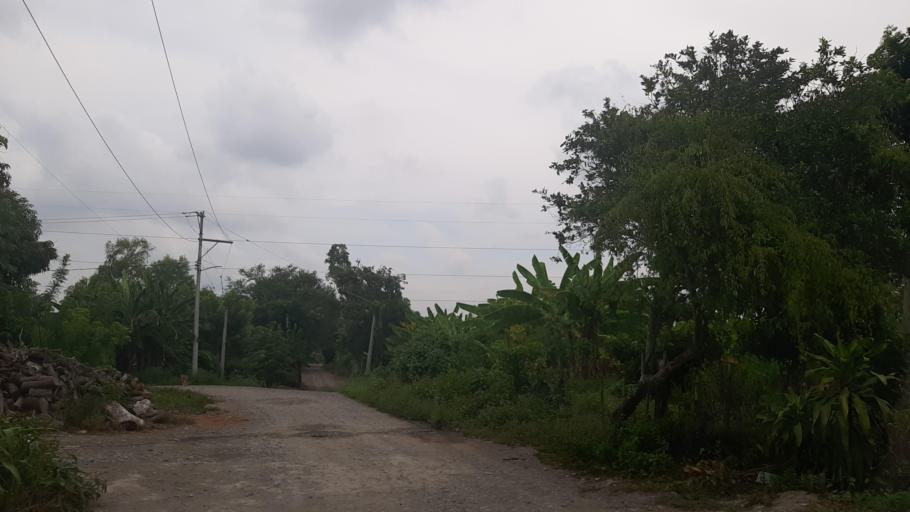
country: MX
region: Veracruz
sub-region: Tihuatlan
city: Ricardo Flores Magon
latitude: 20.5132
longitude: -97.4907
